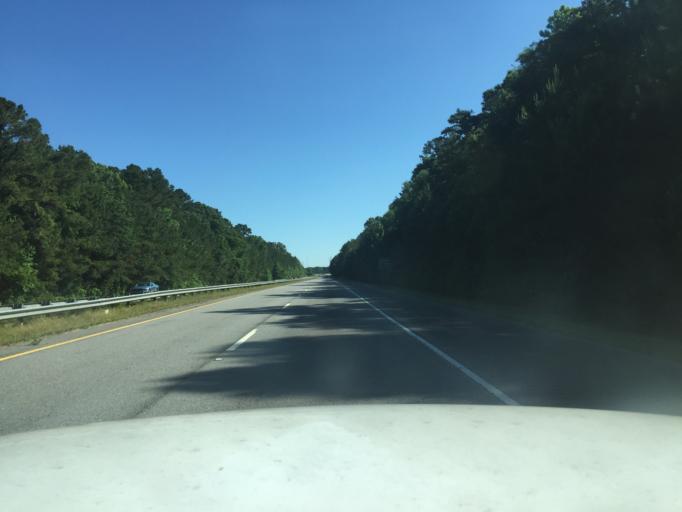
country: US
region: Georgia
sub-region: Chatham County
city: Georgetown
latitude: 32.0288
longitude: -81.1688
